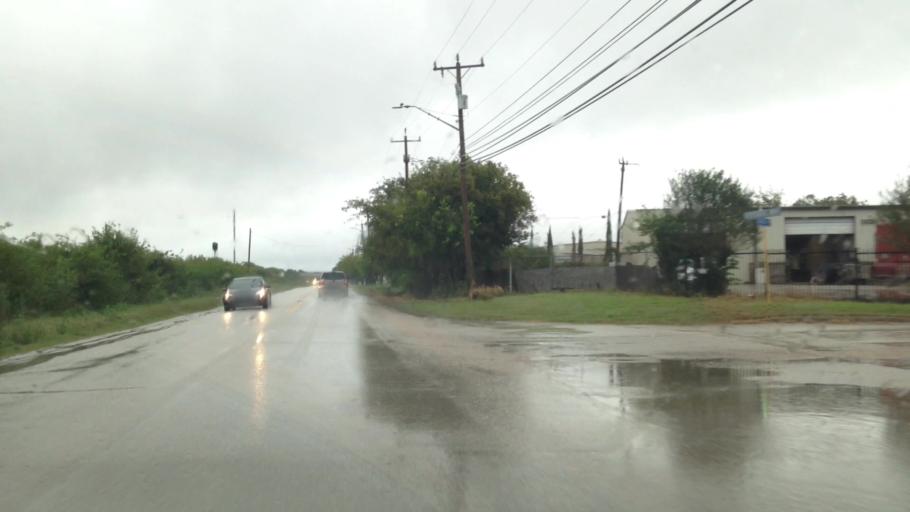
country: US
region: Texas
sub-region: Bexar County
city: Live Oak
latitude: 29.5615
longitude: -98.3727
